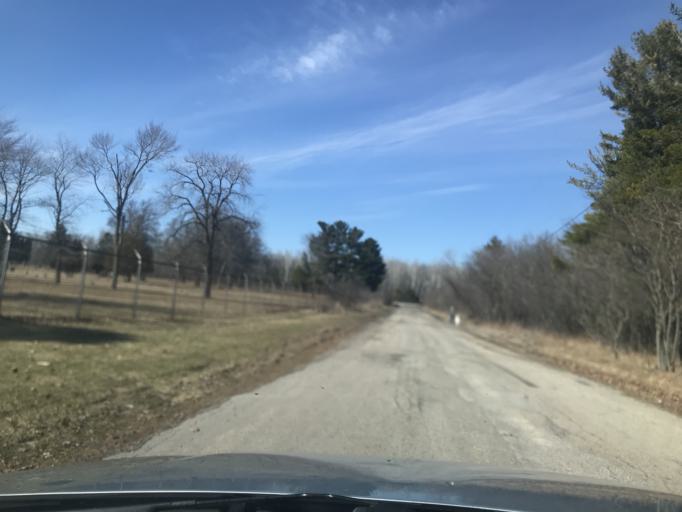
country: US
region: Wisconsin
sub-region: Marinette County
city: Marinette
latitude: 45.1131
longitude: -87.6509
